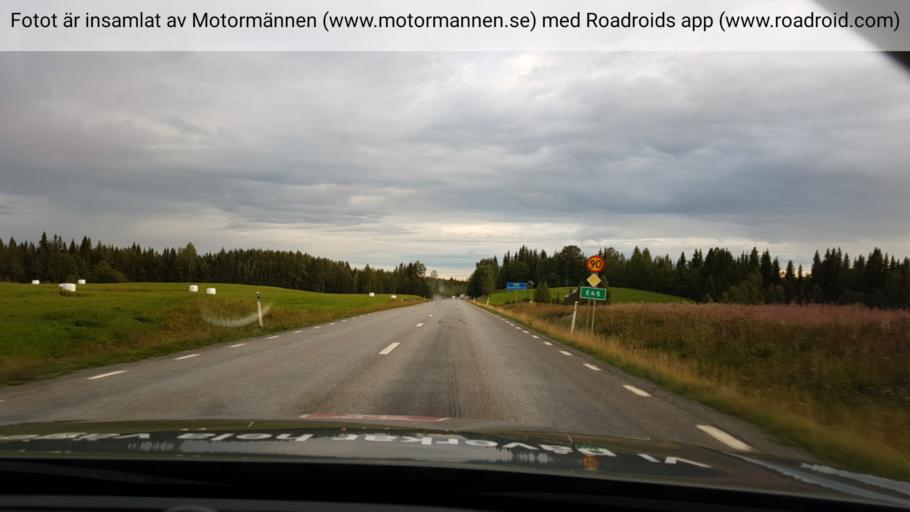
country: SE
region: Jaemtland
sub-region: OEstersunds Kommun
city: Lit
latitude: 63.4348
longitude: 15.1242
